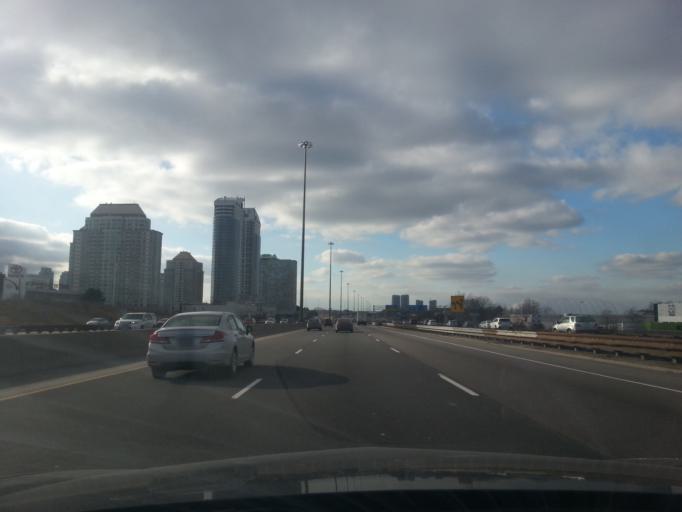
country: CA
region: Ontario
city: Scarborough
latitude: 43.7840
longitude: -79.2409
